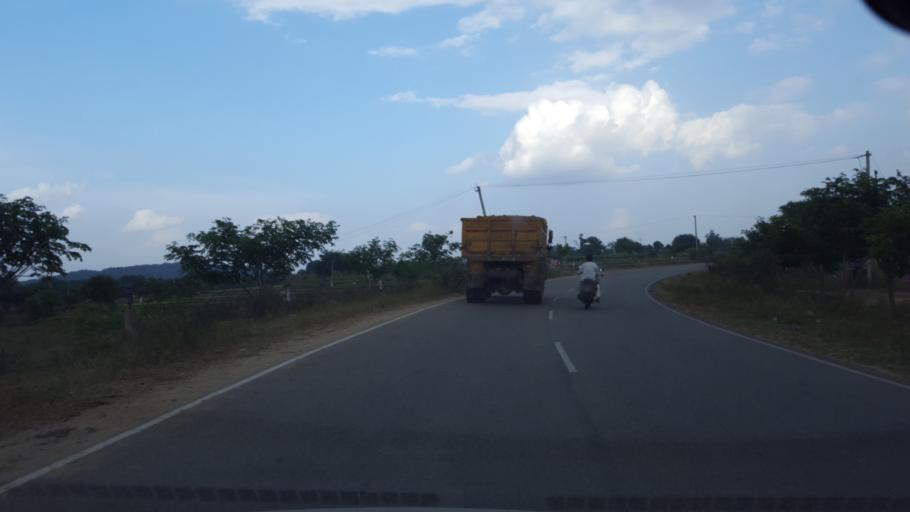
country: IN
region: Telangana
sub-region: Mahbubnagar
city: Mahbubnagar
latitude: 16.7611
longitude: 77.9521
